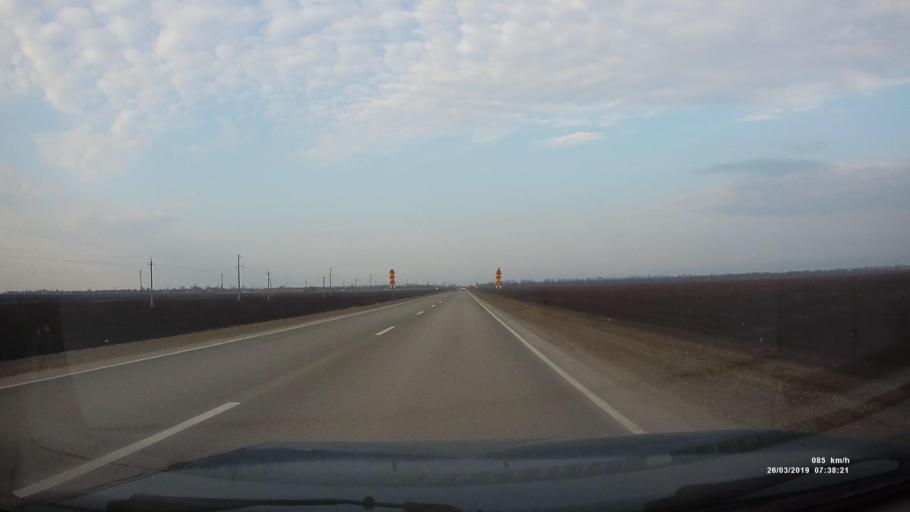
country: RU
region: Rostov
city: Novobessergenovka
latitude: 47.1998
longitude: 38.6842
